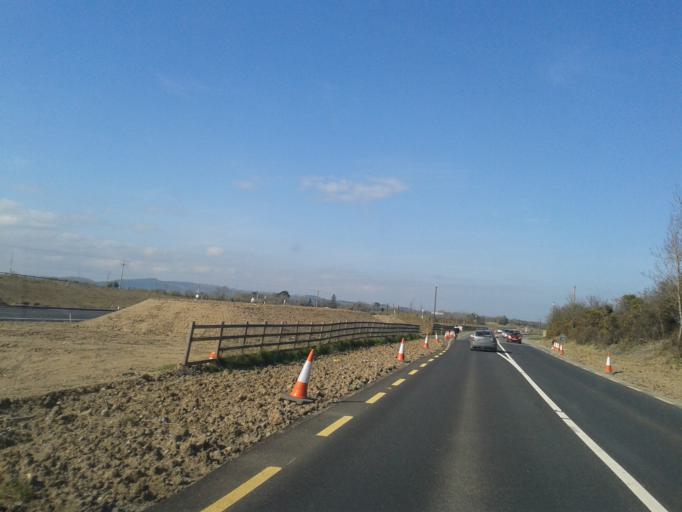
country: IE
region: Leinster
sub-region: Wicklow
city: Arklow
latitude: 52.8608
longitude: -6.1042
